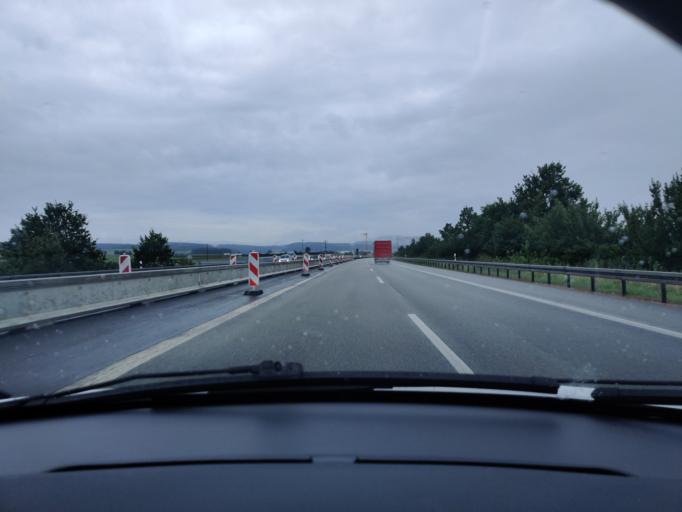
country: DE
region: Bavaria
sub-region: Upper Palatinate
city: Nabburg
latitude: 49.4710
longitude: 12.1937
